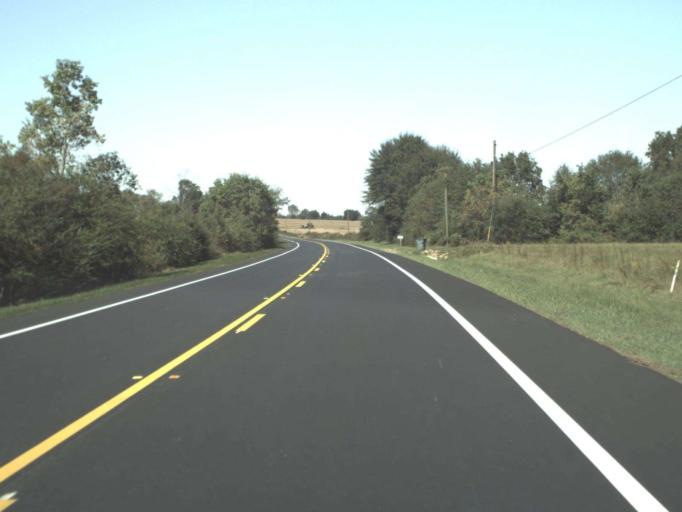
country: US
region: Alabama
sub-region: Covington County
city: Florala
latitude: 30.8714
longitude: -86.2577
